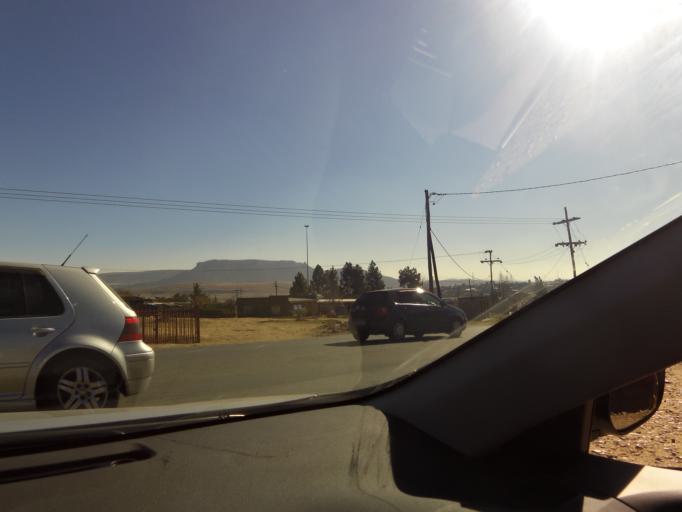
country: LS
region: Maseru
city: Maseru
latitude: -29.2846
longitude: 27.5269
